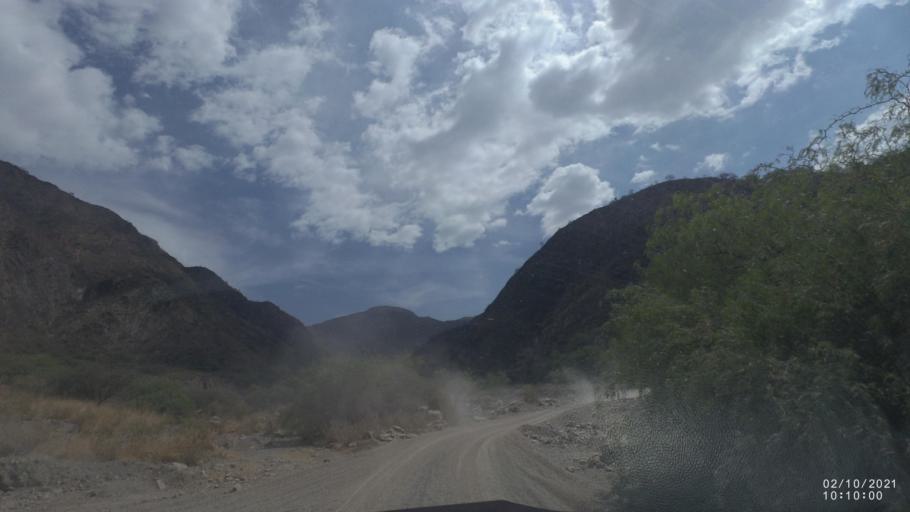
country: BO
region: Cochabamba
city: Irpa Irpa
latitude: -17.7326
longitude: -66.3349
